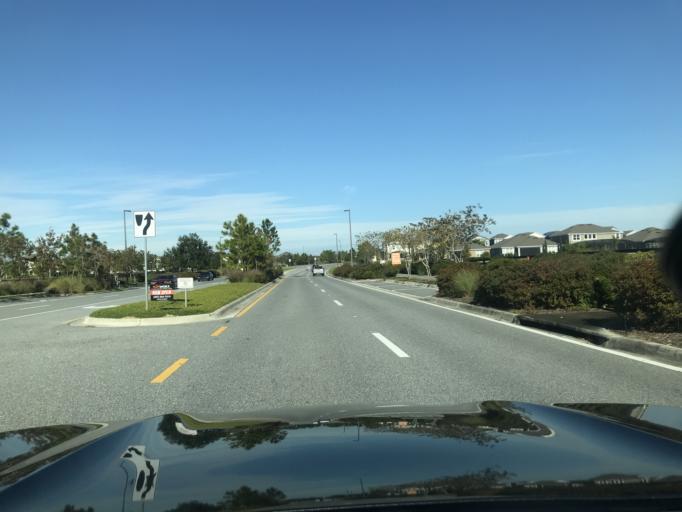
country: US
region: Florida
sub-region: Orange County
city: Lake Butler
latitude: 28.4613
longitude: -81.6245
